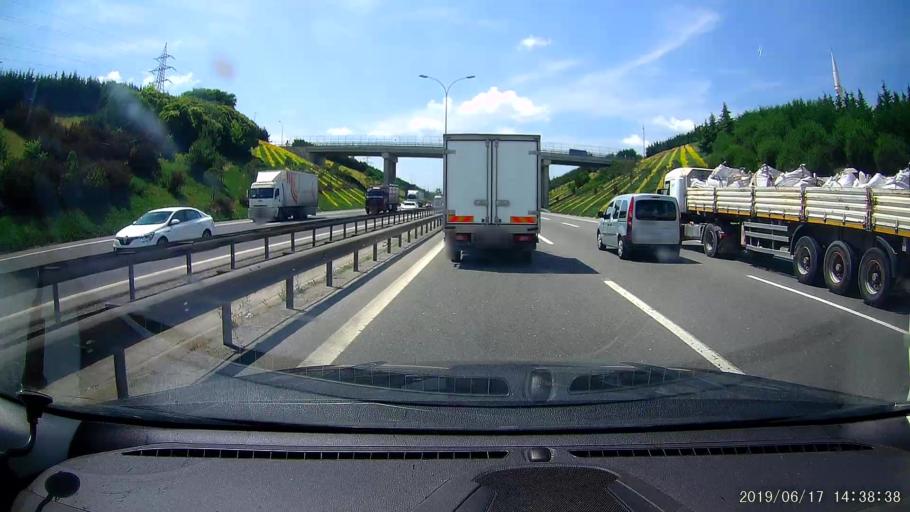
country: TR
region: Istanbul
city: Sultanbeyli
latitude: 40.9518
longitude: 29.3027
